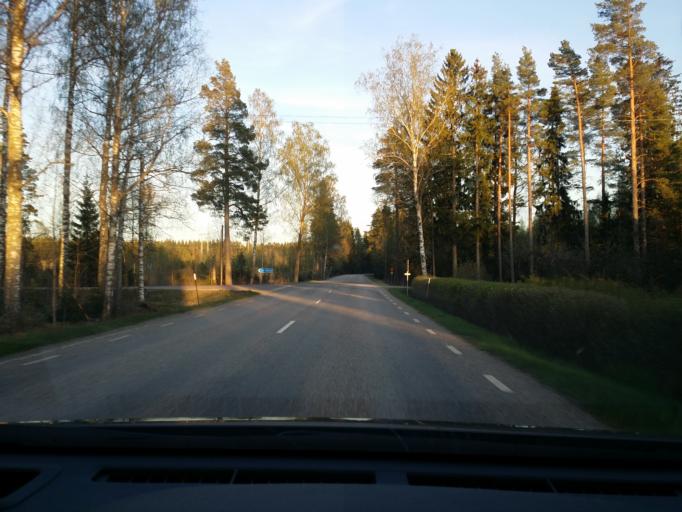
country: SE
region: Vaestmanland
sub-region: Sala Kommun
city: Sala
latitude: 59.8266
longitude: 16.5211
